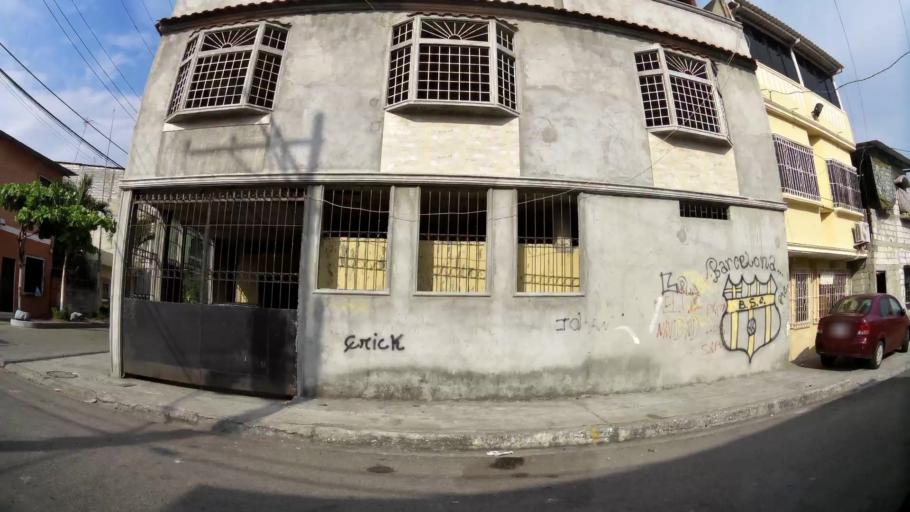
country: EC
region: Guayas
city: Guayaquil
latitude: -2.2515
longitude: -79.9053
